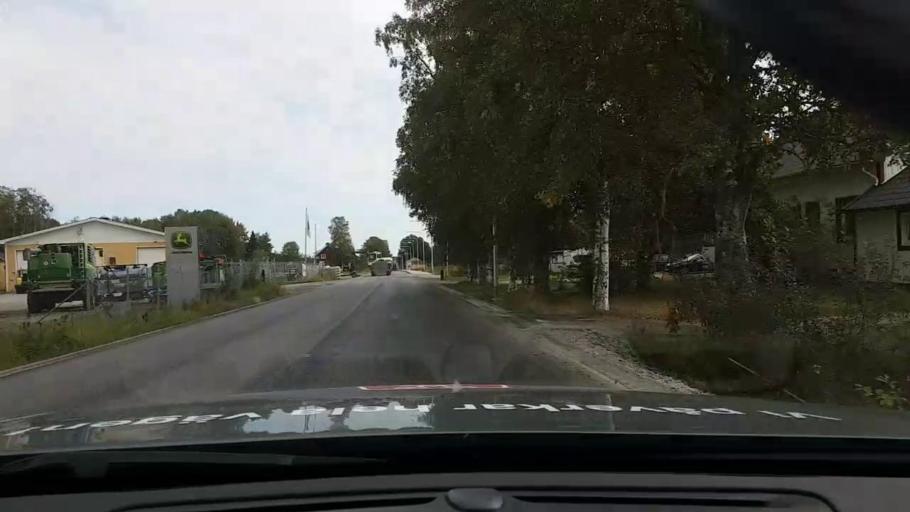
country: SE
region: Vaesternorrland
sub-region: OErnskoeldsviks Kommun
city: Bjasta
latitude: 63.2892
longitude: 18.4403
